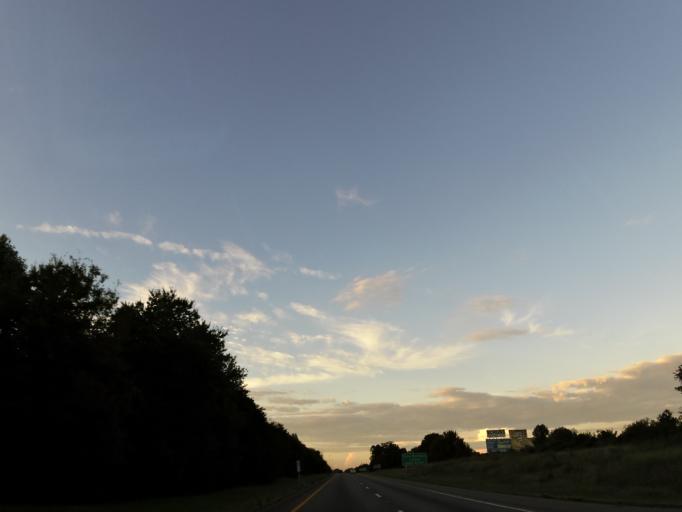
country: US
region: Tennessee
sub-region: McMinn County
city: Athens
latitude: 35.4565
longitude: -84.6579
